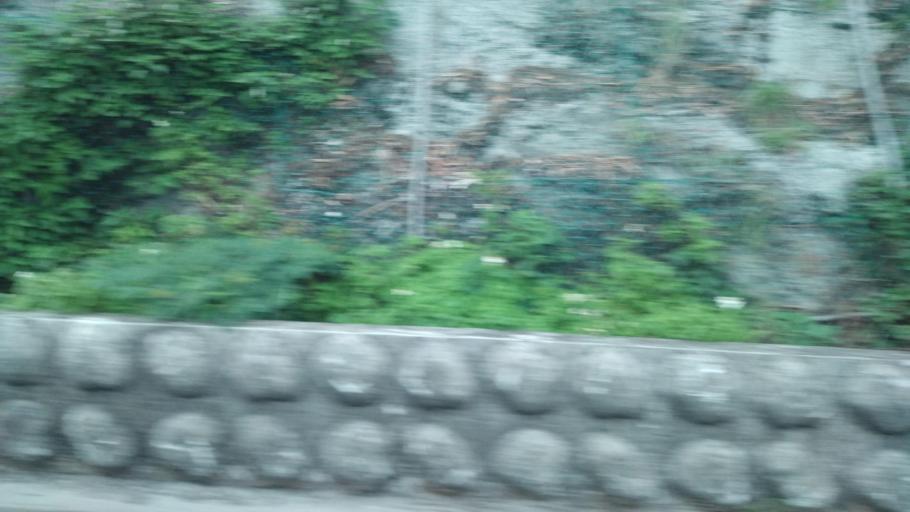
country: TW
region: Taiwan
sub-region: Hualien
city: Hualian
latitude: 24.2255
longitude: 121.7042
